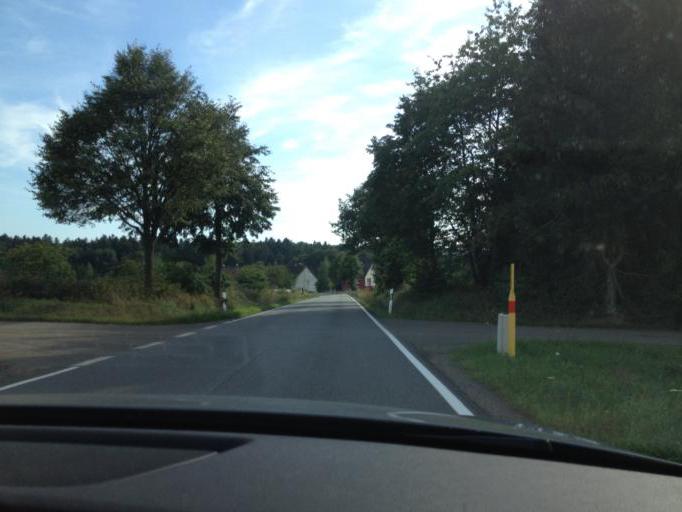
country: DE
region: Rheinland-Pfalz
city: Breitenbach
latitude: 49.4234
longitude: 7.2843
